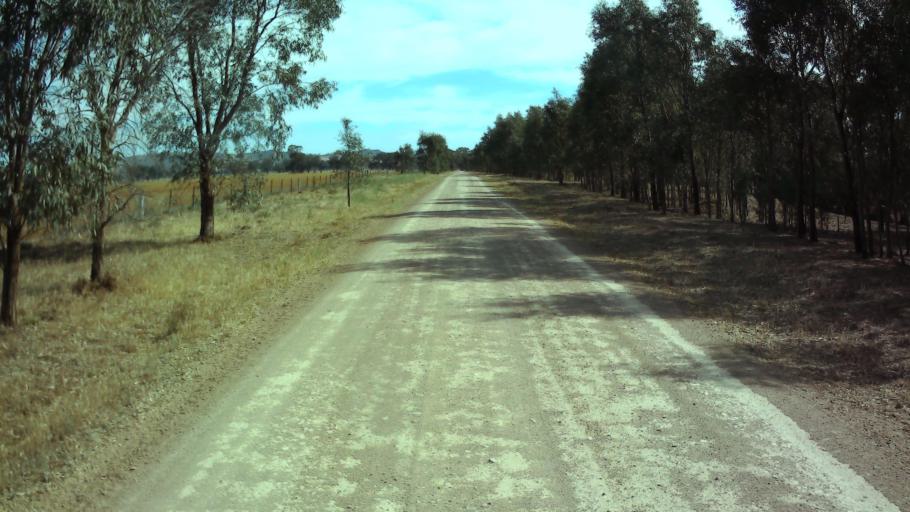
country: AU
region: New South Wales
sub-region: Weddin
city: Grenfell
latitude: -33.7086
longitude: 148.3007
